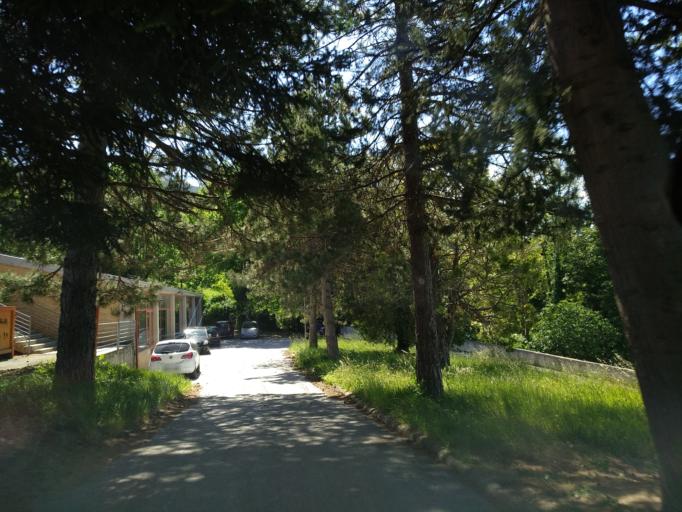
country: IT
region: The Marches
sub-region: Provincia di Pesaro e Urbino
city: Urbino
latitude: 43.7356
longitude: 12.6291
